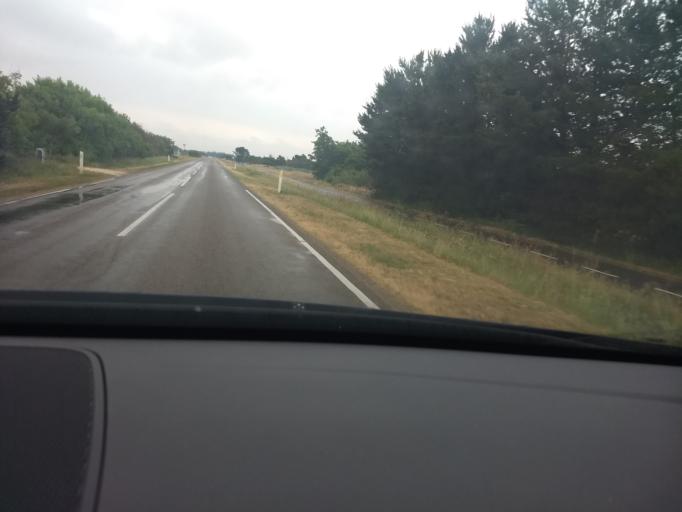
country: DK
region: South Denmark
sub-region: Fano Kommune
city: Nordby
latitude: 55.4175
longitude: 8.3996
